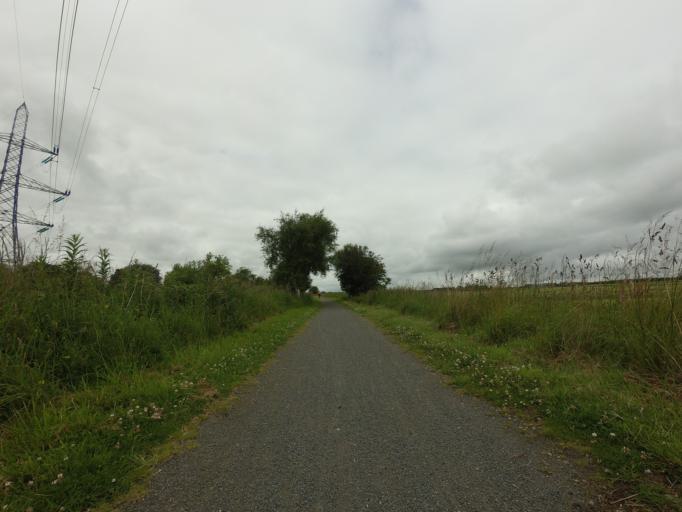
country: GB
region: Scotland
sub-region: Aberdeenshire
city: Mintlaw
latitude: 57.4924
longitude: -2.1357
